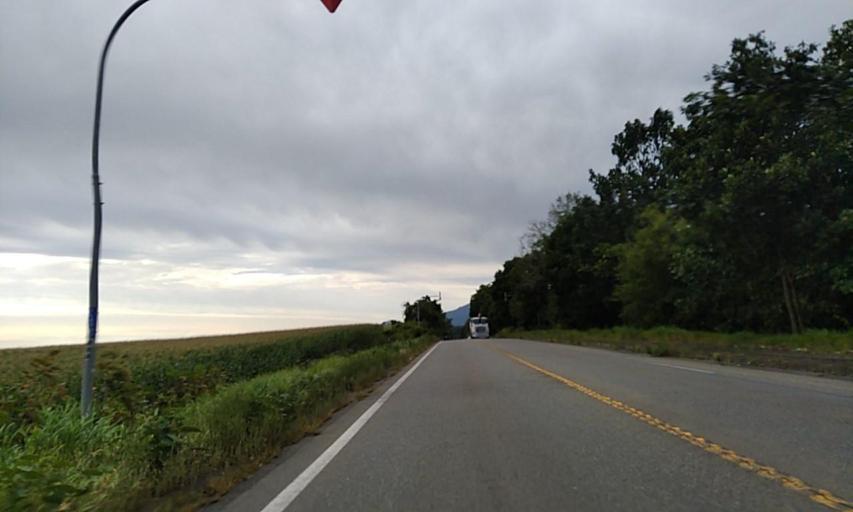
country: JP
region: Hokkaido
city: Otofuke
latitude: 42.9826
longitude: 142.8916
